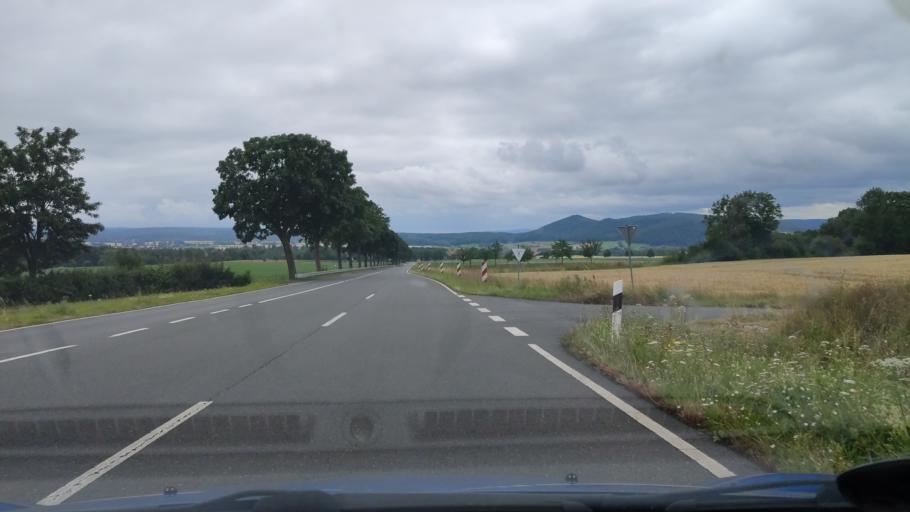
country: DE
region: Lower Saxony
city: Holenberg
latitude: 51.9056
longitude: 9.6049
